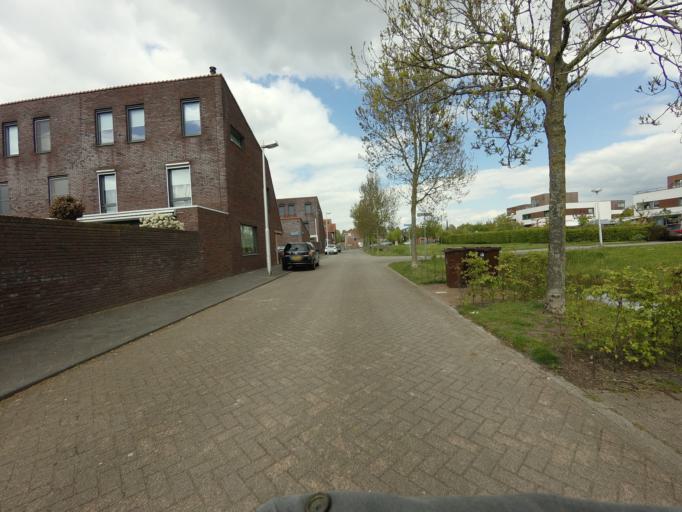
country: NL
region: Utrecht
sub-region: Stichtse Vecht
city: Maarssen
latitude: 52.0846
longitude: 5.0595
